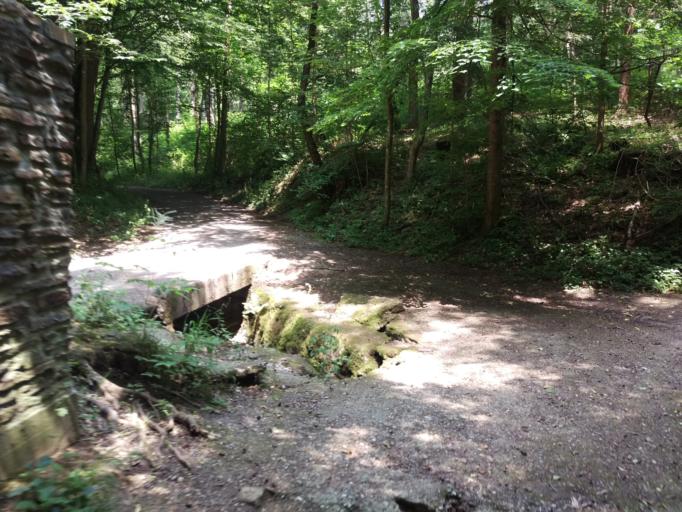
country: AT
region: Styria
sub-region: Graz Stadt
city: Mariatrost
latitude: 47.1105
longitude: 15.4823
